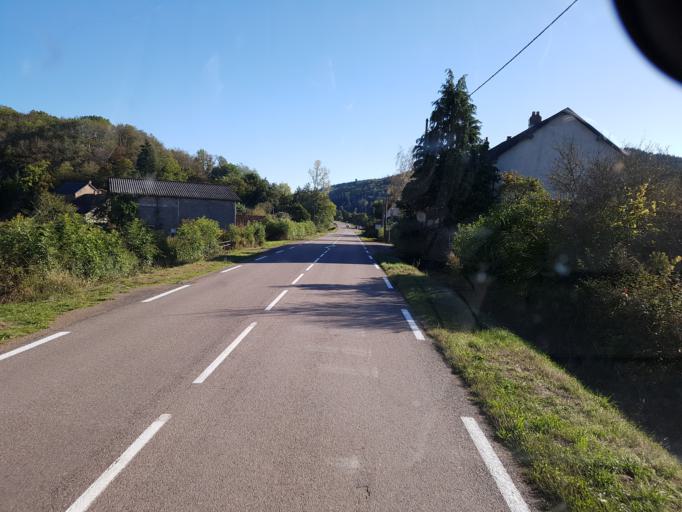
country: FR
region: Bourgogne
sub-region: Departement de Saone-et-Loire
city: Autun
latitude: 47.1008
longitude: 4.2310
